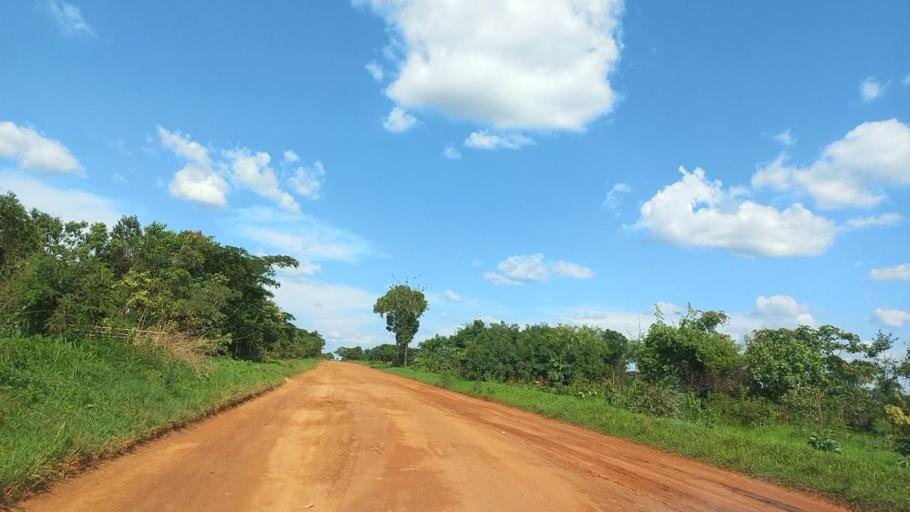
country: ZM
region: Copperbelt
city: Kitwe
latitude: -12.8686
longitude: 28.3639
